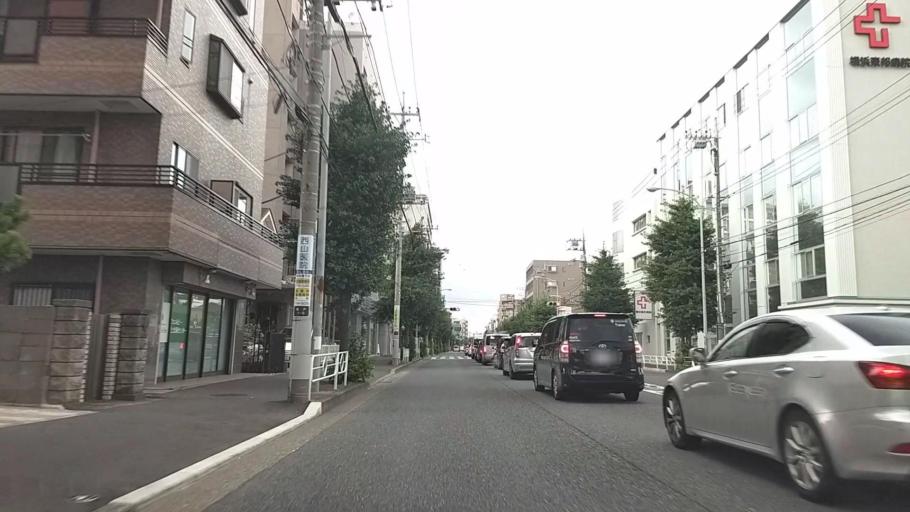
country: JP
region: Kanagawa
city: Yokohama
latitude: 35.4141
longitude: 139.5973
